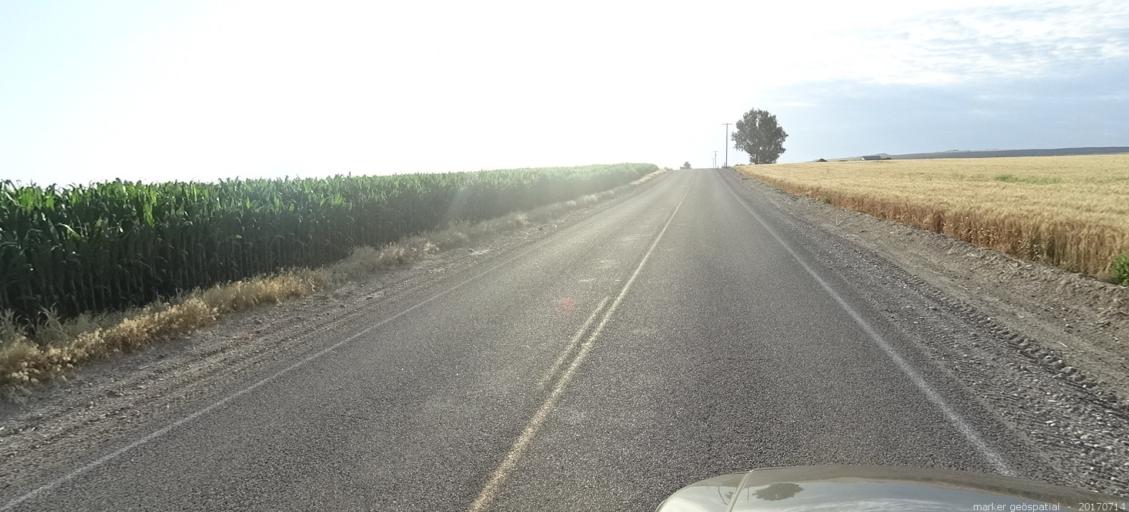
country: US
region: Idaho
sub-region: Ada County
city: Kuna
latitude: 43.4593
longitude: -116.5103
